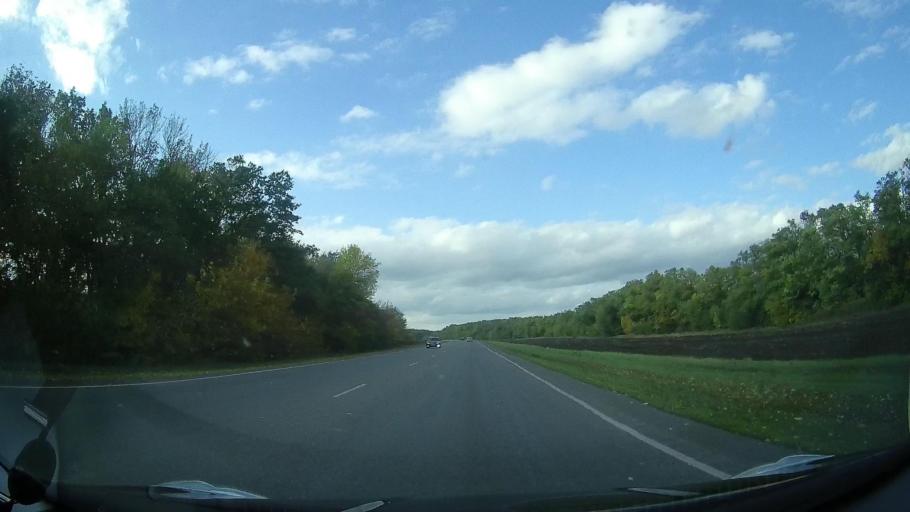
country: RU
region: Rostov
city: Kirovskaya
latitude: 46.9576
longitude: 40.0763
